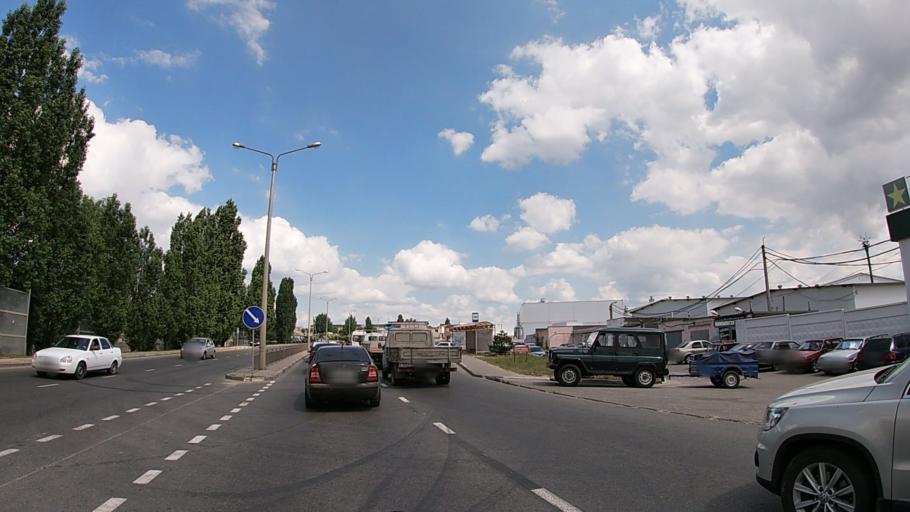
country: RU
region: Belgorod
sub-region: Belgorodskiy Rayon
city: Belgorod
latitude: 50.6102
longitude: 36.5339
